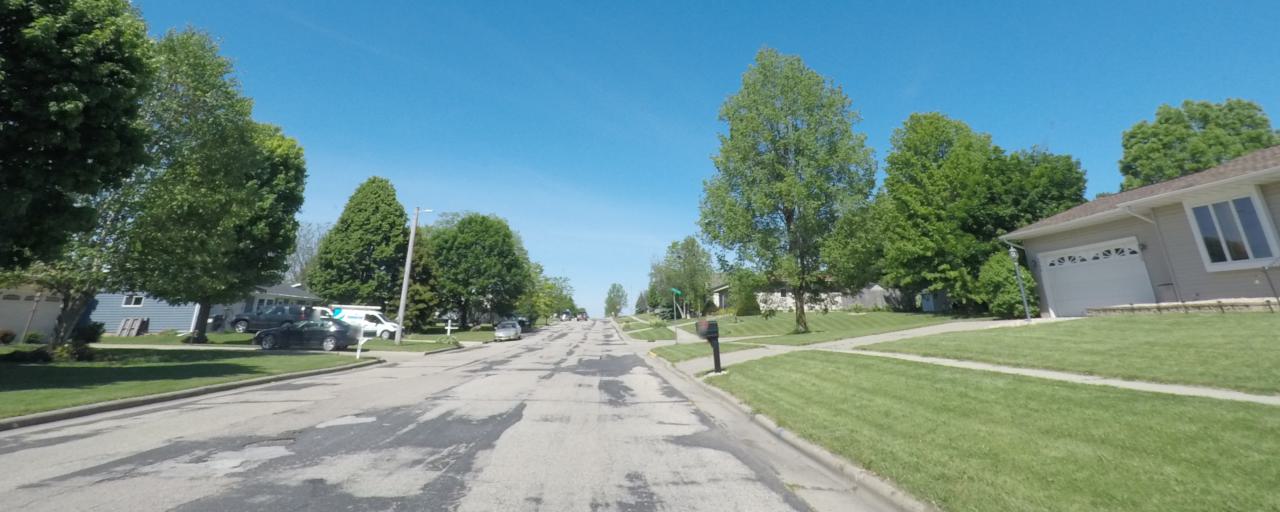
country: US
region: Wisconsin
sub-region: Rock County
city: Evansville
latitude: 42.7822
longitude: -89.3145
